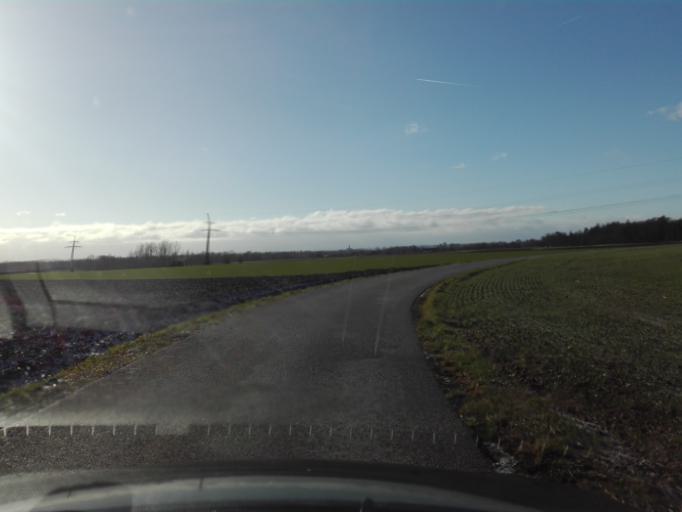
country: AT
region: Upper Austria
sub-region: Politischer Bezirk Perg
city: Bad Kreuzen
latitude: 48.2016
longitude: 14.7614
